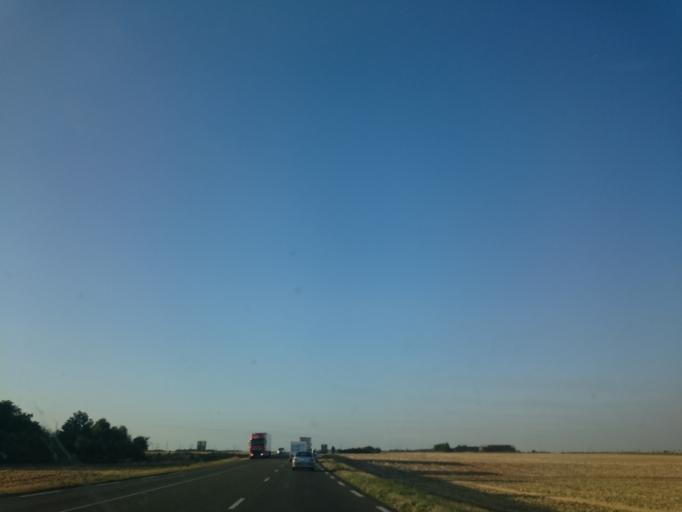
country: FR
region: Ile-de-France
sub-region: Departement de l'Essonne
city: Angerville
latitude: 48.2835
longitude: 1.9791
